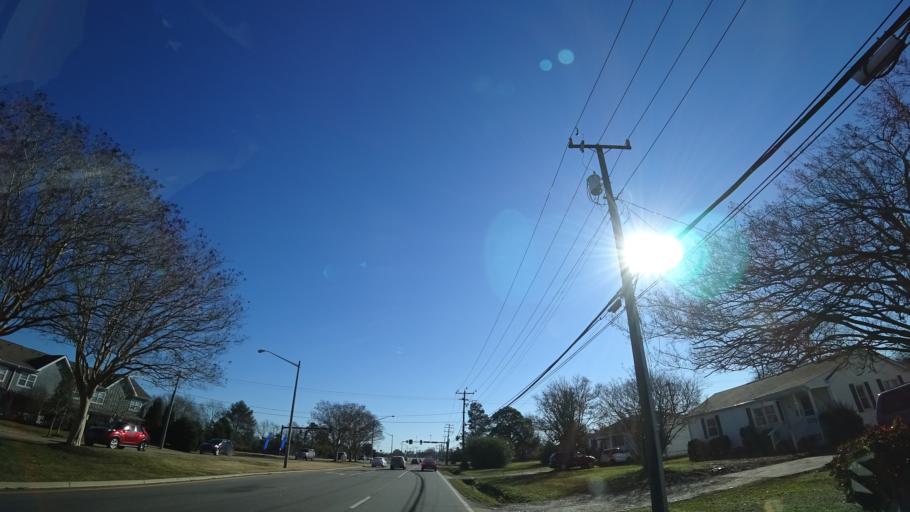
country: US
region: Virginia
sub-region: City of Hampton
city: Hampton
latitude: 37.0374
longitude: -76.3704
